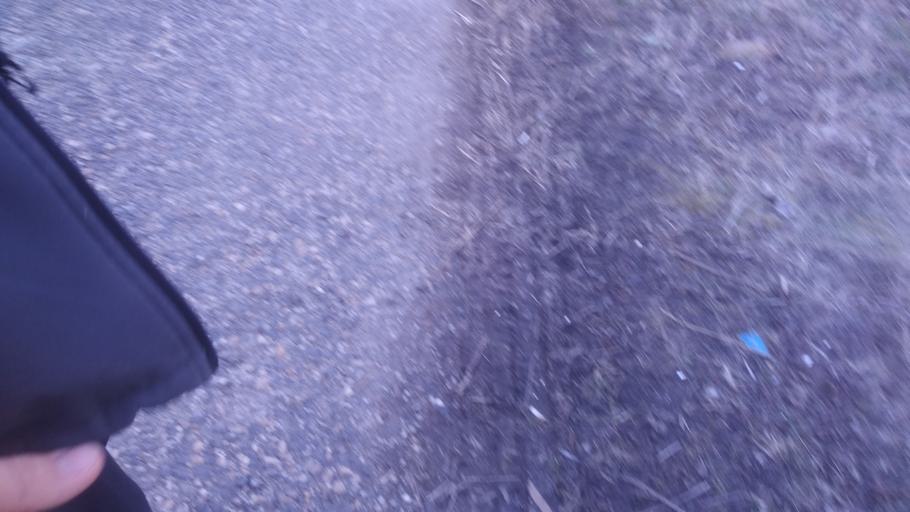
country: HU
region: Komarom-Esztergom
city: Baj
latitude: 47.6450
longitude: 18.3571
